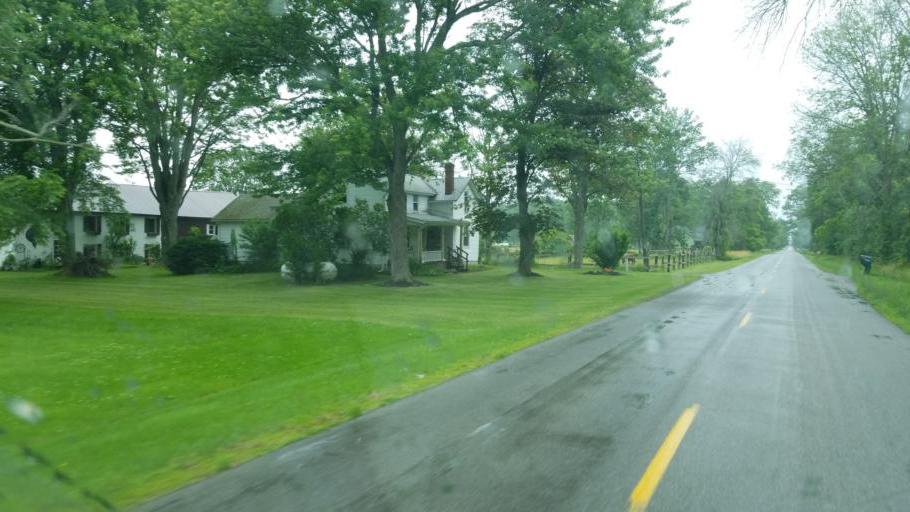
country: US
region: New York
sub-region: Niagara County
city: Wilson
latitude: 43.2644
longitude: -78.8355
